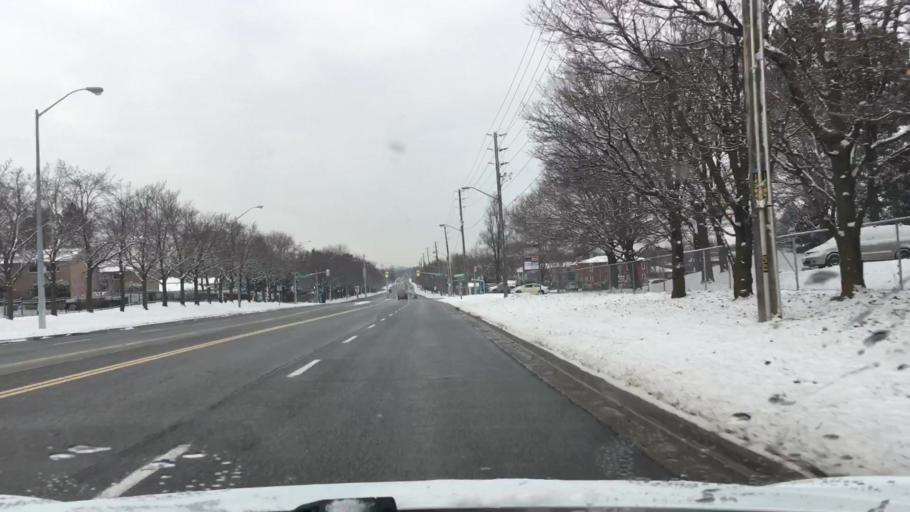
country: CA
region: Ontario
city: Markham
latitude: 43.8784
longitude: -79.2413
